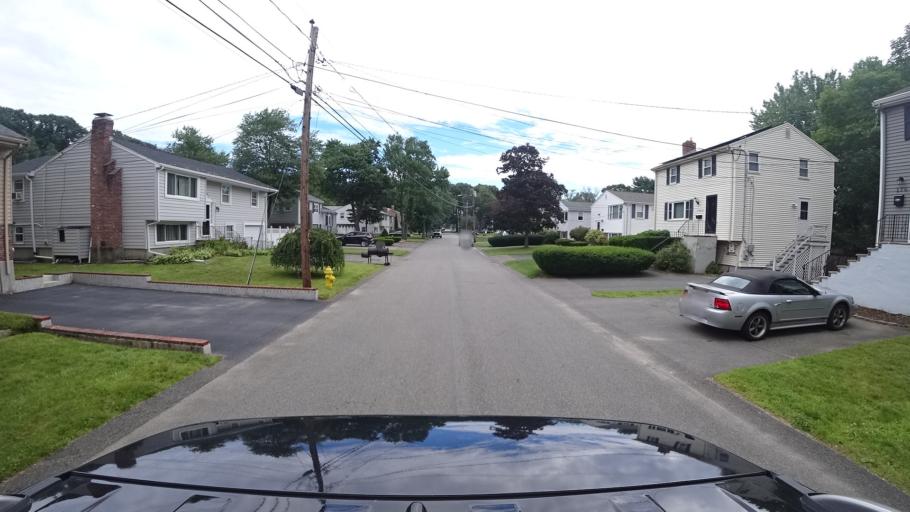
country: US
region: Massachusetts
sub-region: Norfolk County
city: Dedham
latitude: 42.2266
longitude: -71.1479
